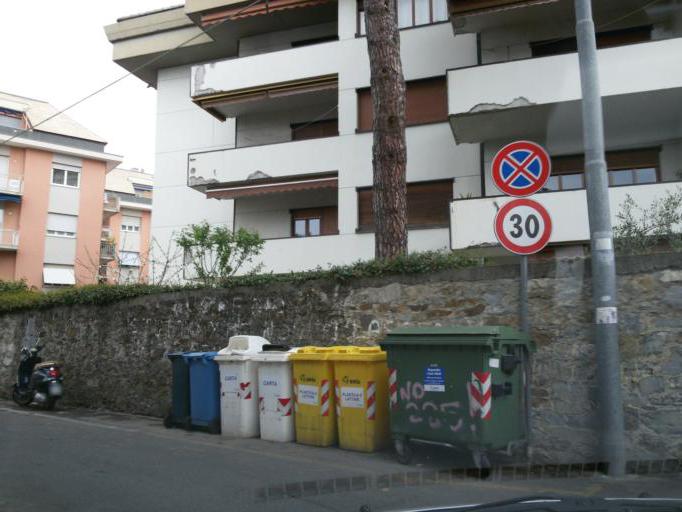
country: IT
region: Liguria
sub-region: Provincia di Genova
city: Genoa
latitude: 44.4015
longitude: 8.9749
